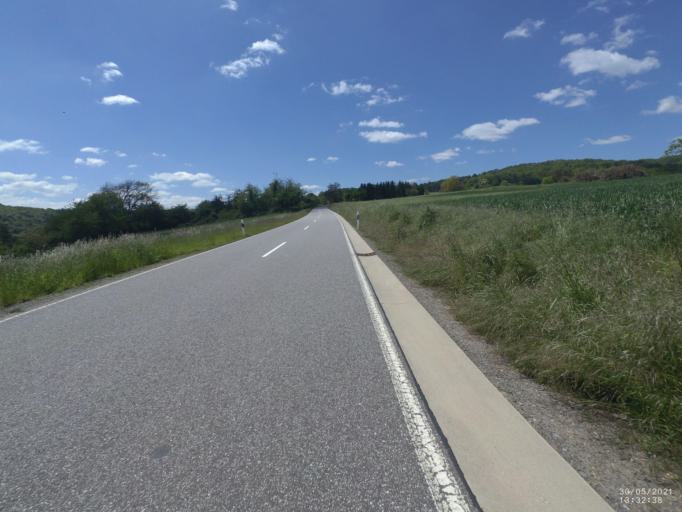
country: DE
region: Rheinland-Pfalz
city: Rhens
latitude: 50.2839
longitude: 7.5965
